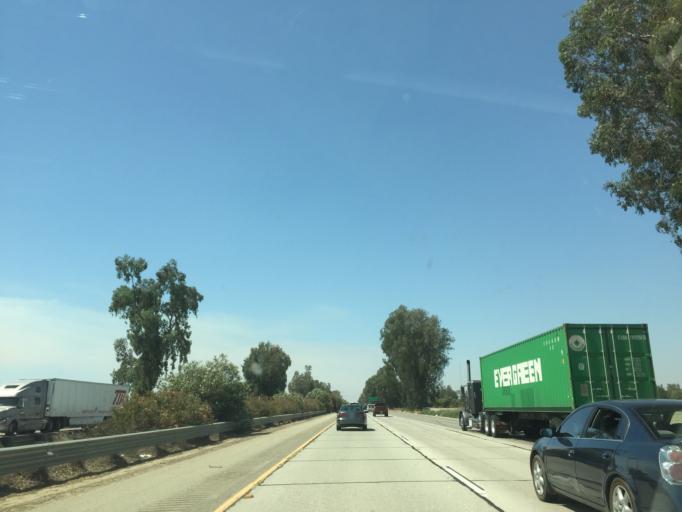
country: US
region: California
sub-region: Kern County
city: Greenfield
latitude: 35.1871
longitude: -119.0068
